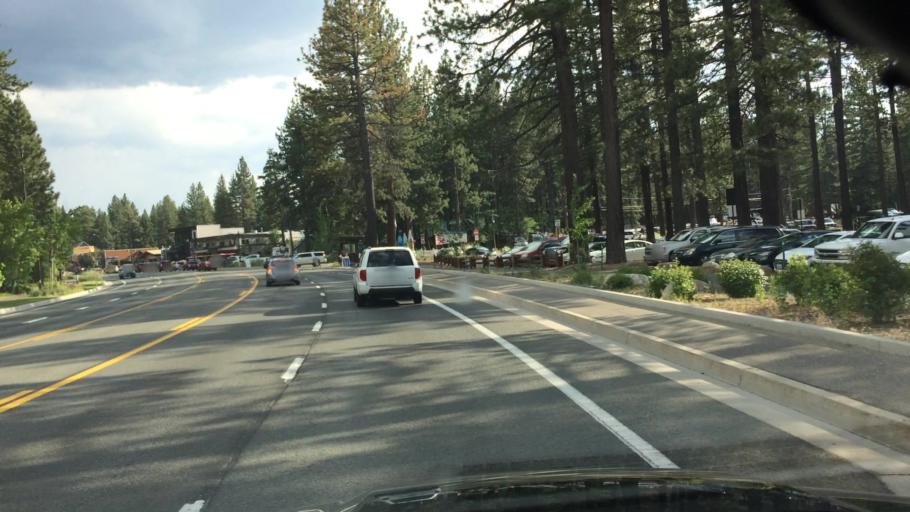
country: US
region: California
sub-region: El Dorado County
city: South Lake Tahoe
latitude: 38.9437
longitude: -119.9768
